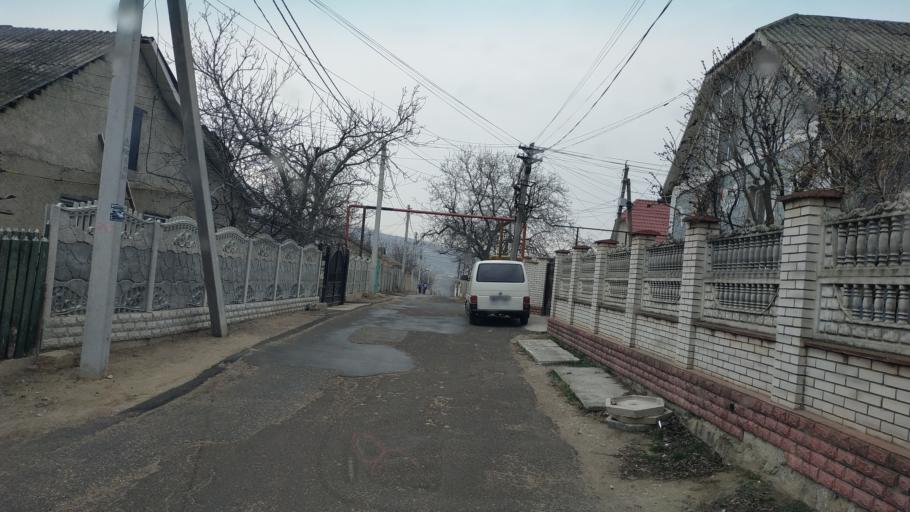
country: MD
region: Chisinau
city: Singera
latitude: 46.9165
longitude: 28.9599
